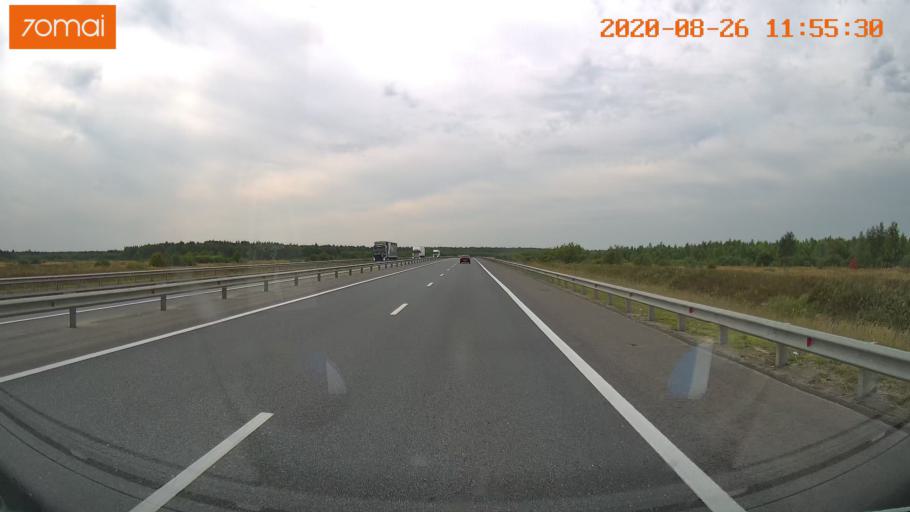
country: RU
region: Rjazan
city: Kiritsy
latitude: 54.2722
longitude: 40.3948
